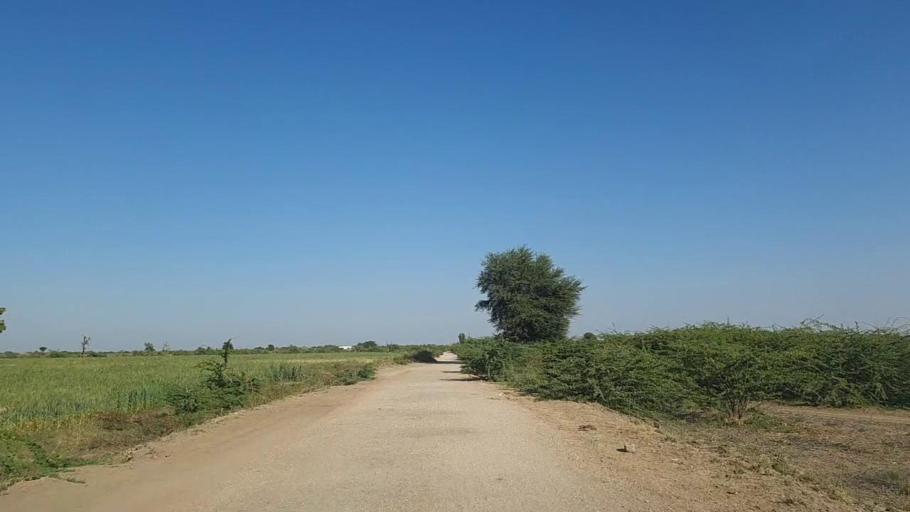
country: PK
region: Sindh
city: Samaro
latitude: 25.2490
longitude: 69.4918
